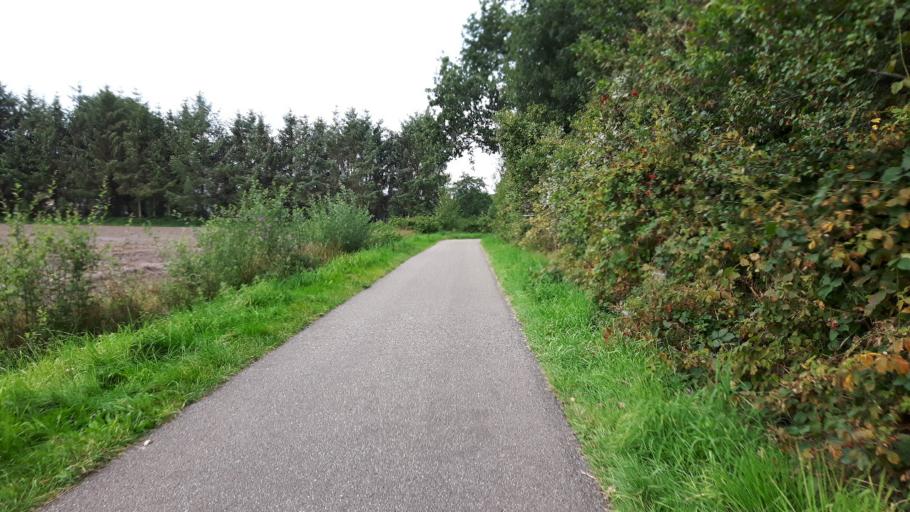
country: NL
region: Groningen
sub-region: Gemeente Leek
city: Leek
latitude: 53.1096
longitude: 6.4359
